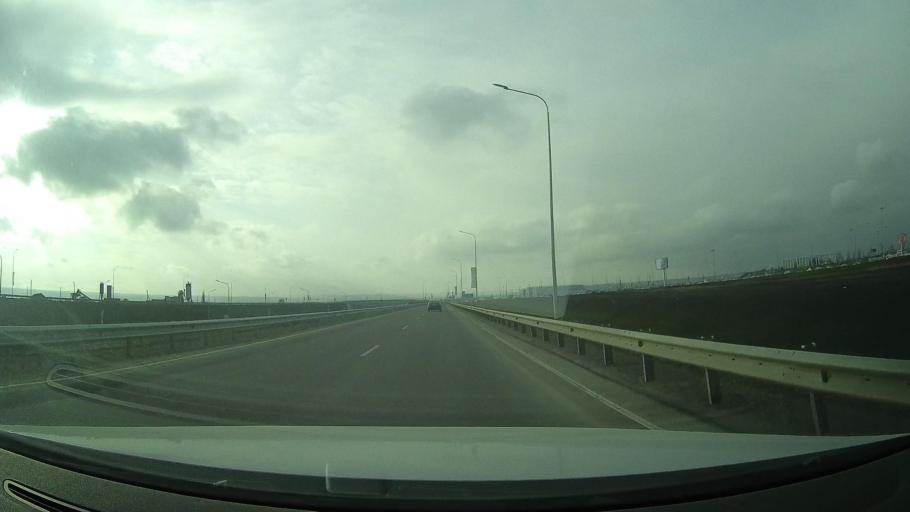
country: RU
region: Rostov
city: Grushevskaya
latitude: 47.4856
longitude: 39.9332
